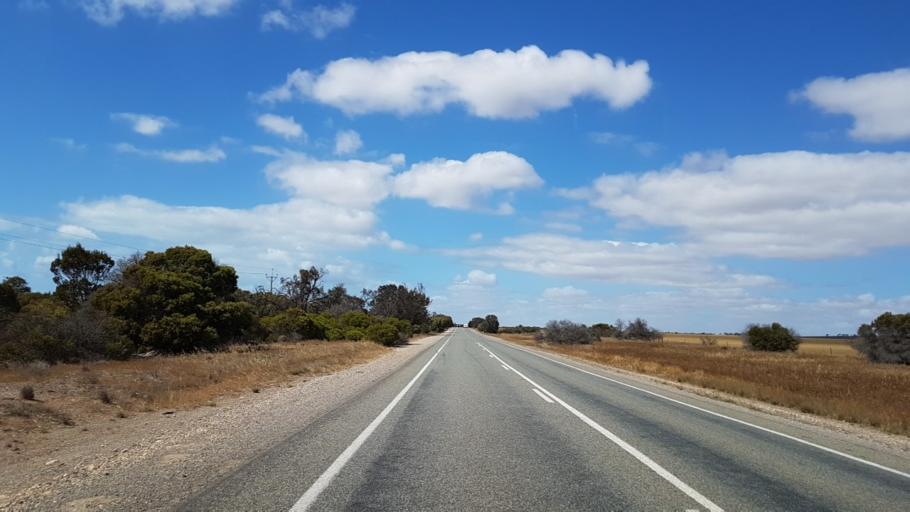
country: AU
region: South Australia
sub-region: Yorke Peninsula
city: Ardrossan
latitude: -34.2631
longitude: 137.9893
